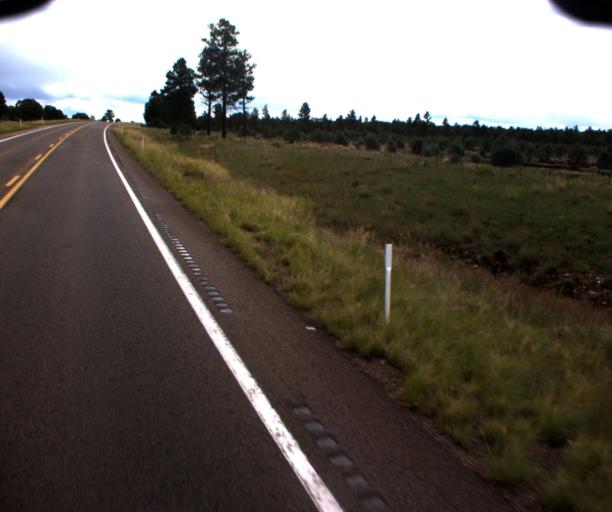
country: US
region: Arizona
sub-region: Navajo County
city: Heber-Overgaard
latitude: 34.3928
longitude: -110.5129
